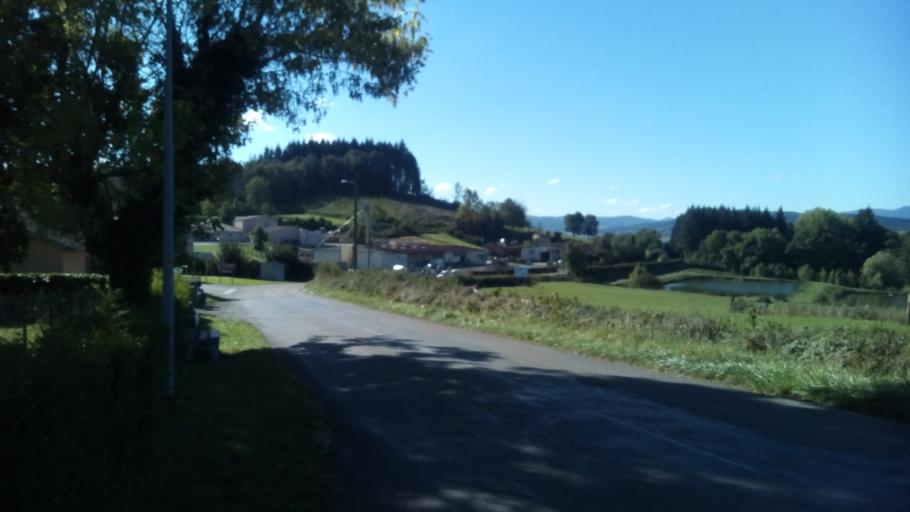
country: FR
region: Bourgogne
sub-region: Departement de Saone-et-Loire
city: Matour
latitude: 46.3025
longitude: 4.6031
